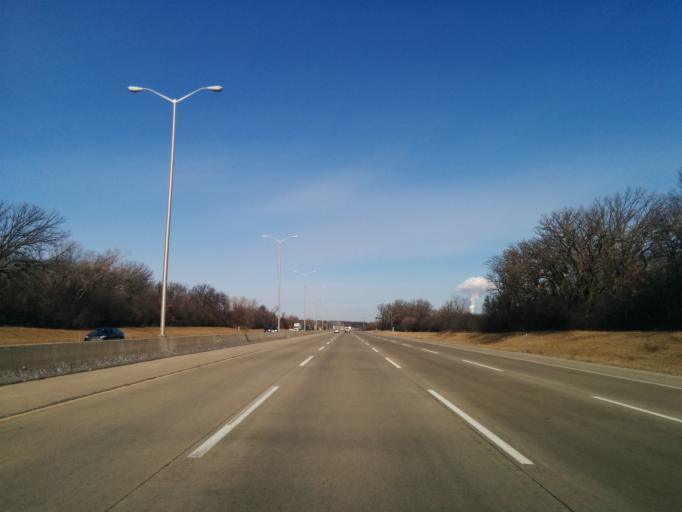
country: US
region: Illinois
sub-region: Lake County
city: Wadsworth
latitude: 42.4034
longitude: -87.9484
